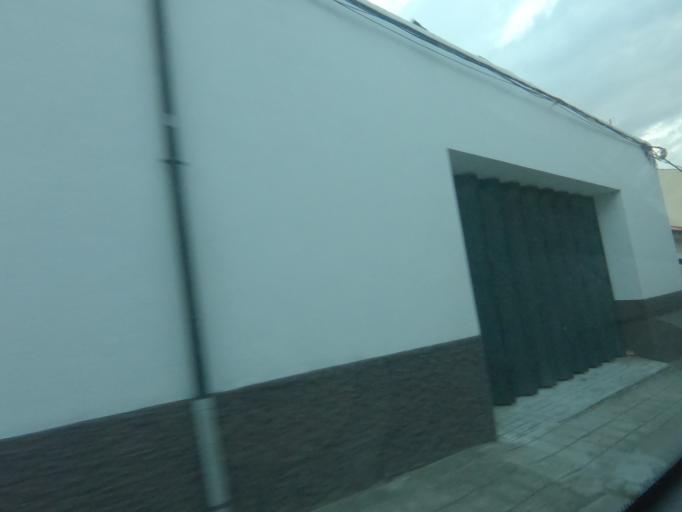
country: PT
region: Vila Real
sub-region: Mesao Frio
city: Mesao Frio
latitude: 41.2119
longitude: -7.9274
